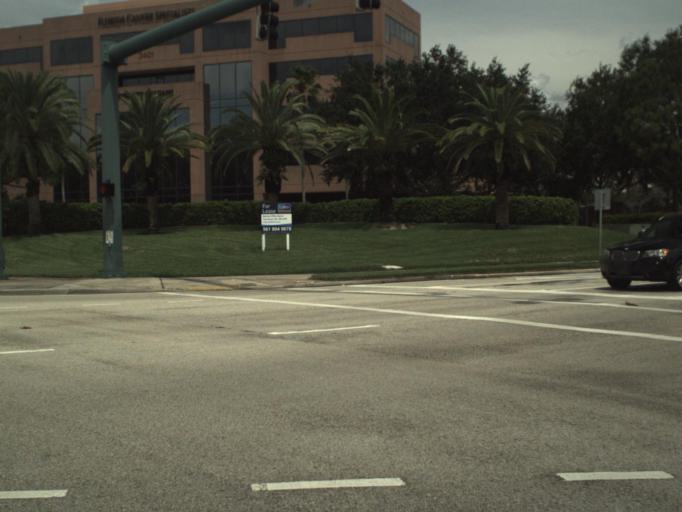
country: US
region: Florida
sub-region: Palm Beach County
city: North Palm Beach
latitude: 26.8452
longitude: -80.0885
